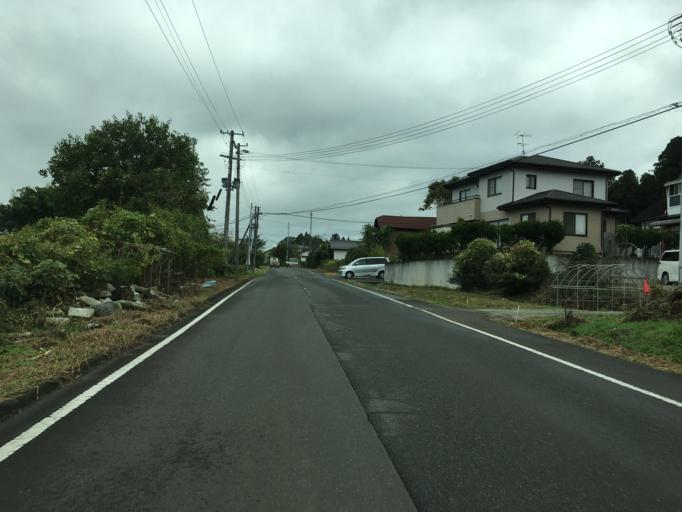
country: JP
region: Fukushima
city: Nihommatsu
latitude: 37.6212
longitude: 140.4418
